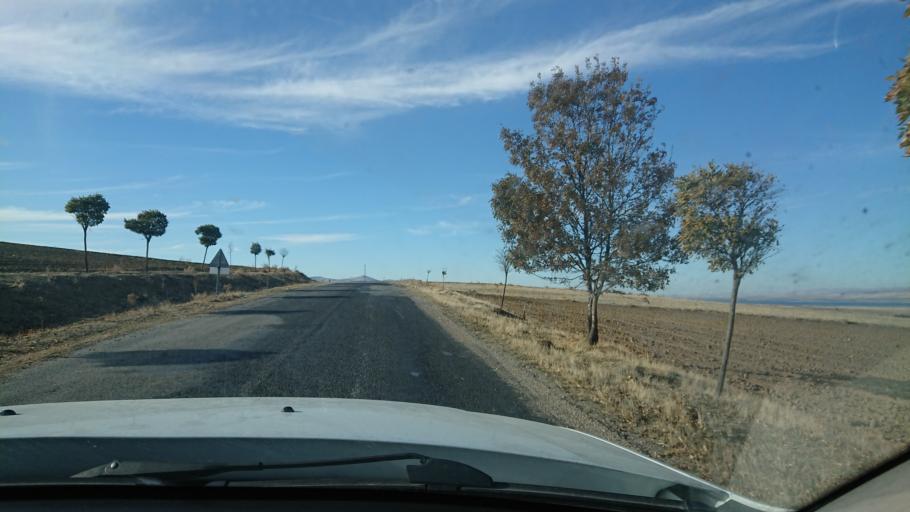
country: TR
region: Aksaray
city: Sariyahsi
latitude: 38.9717
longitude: 33.8647
